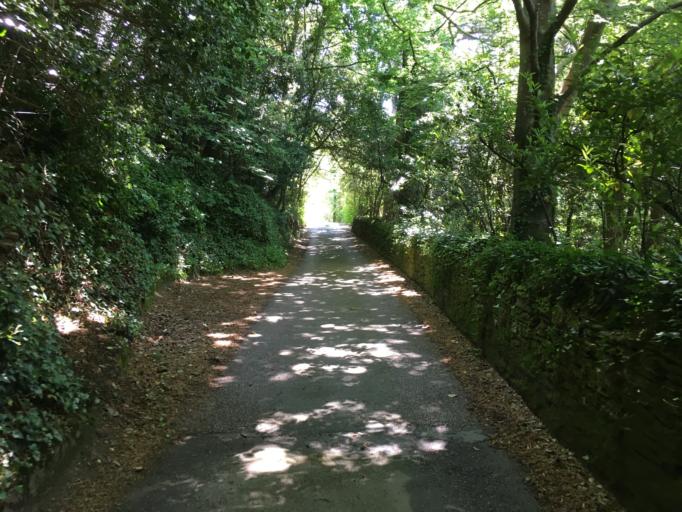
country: GB
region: England
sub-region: Devon
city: Dartmouth
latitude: 50.3465
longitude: -3.5652
